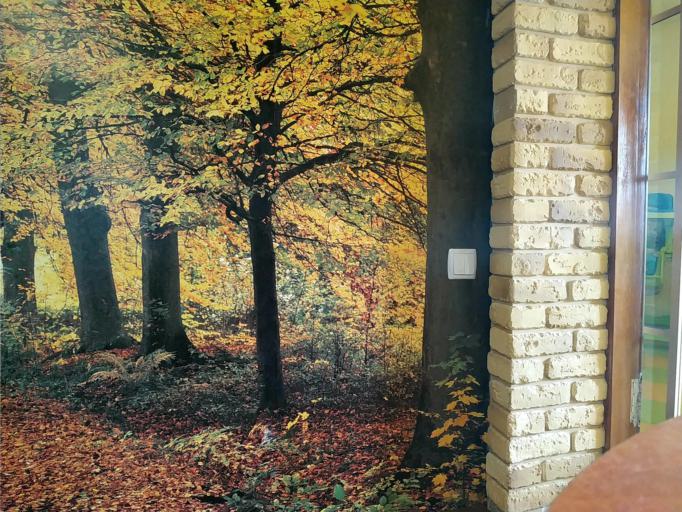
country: RU
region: Smolensk
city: Katyn'
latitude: 54.8875
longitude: 31.7982
